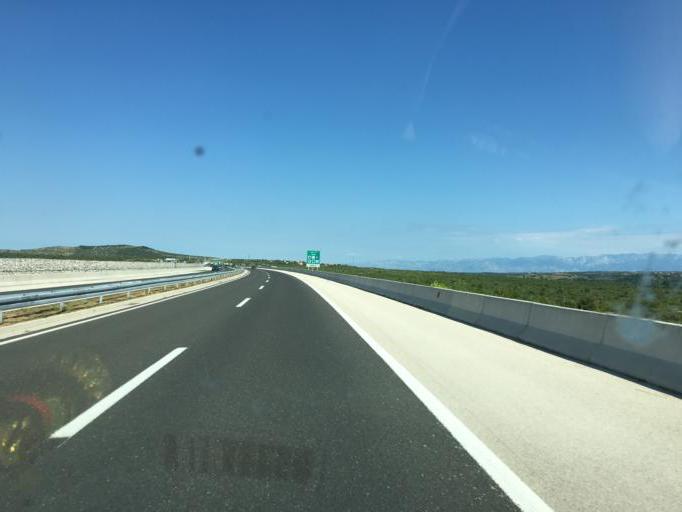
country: HR
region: Zadarska
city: Polaca
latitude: 44.0534
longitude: 15.5430
